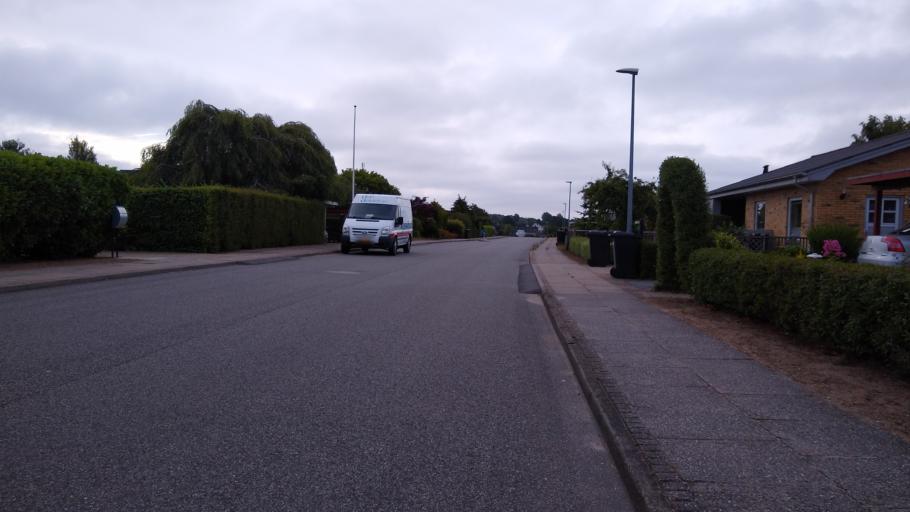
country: DK
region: South Denmark
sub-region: Vejle Kommune
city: Brejning
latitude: 55.6619
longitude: 9.6698
